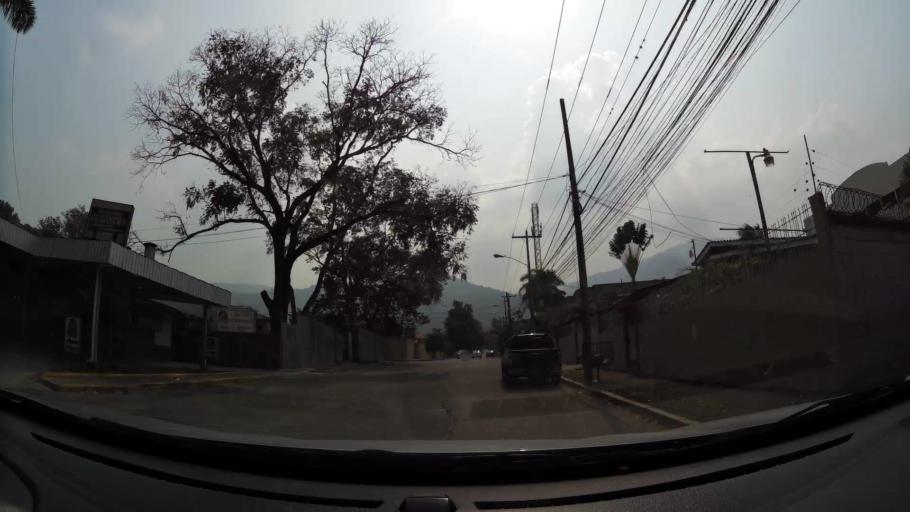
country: HN
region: Cortes
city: Armenta
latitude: 15.4984
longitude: -88.0415
